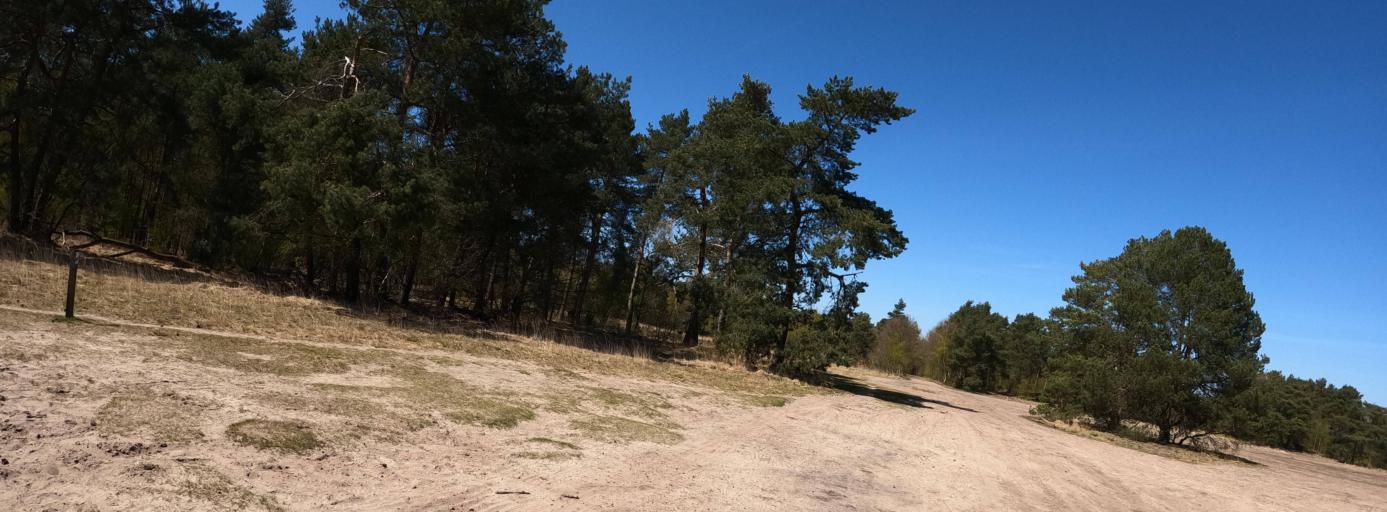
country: BE
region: Flanders
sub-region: Provincie Antwerpen
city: Kalmthout
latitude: 51.3612
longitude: 4.4876
